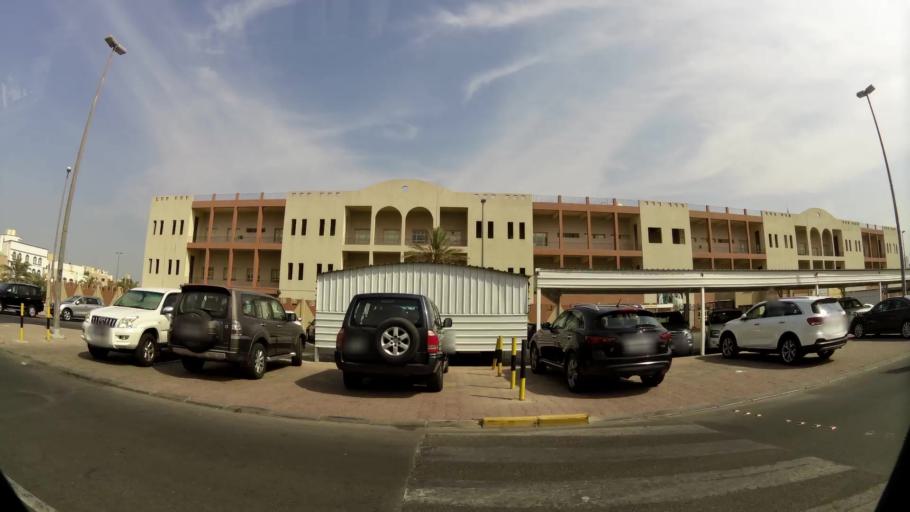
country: KW
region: Al Asimah
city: Ash Shamiyah
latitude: 29.3402
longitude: 47.9782
